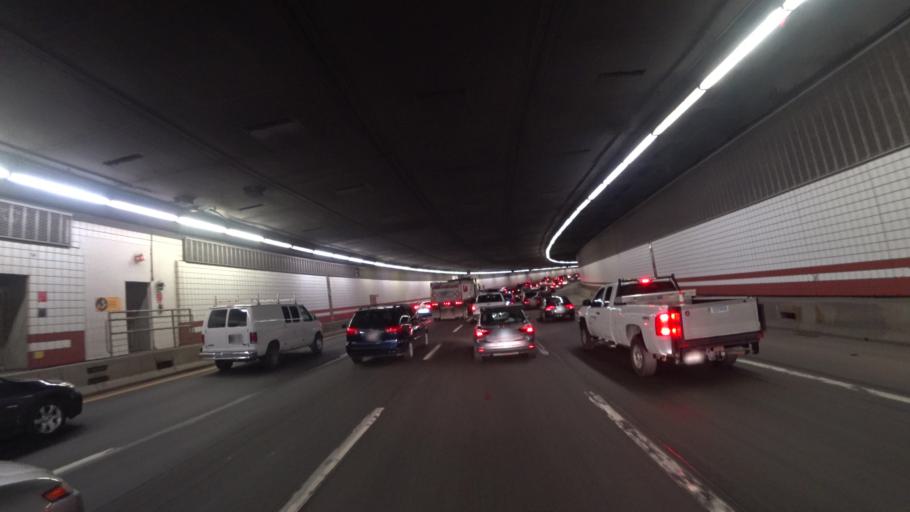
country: US
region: Massachusetts
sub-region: Suffolk County
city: Boston
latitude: 42.3547
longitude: -71.0557
